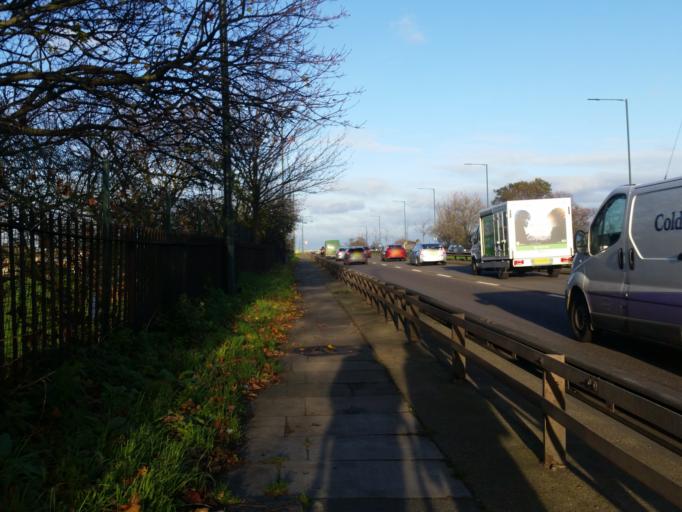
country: GB
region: England
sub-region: Greater London
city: Enfield
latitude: 51.6363
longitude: -0.0678
